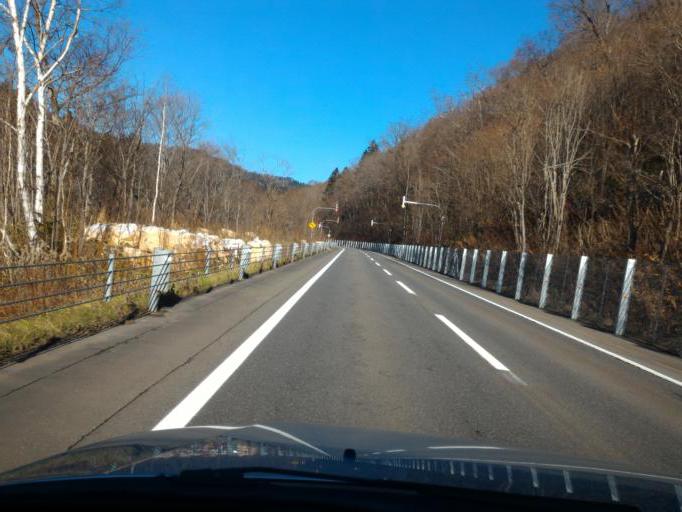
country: JP
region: Hokkaido
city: Ashibetsu
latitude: 43.3401
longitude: 142.1533
